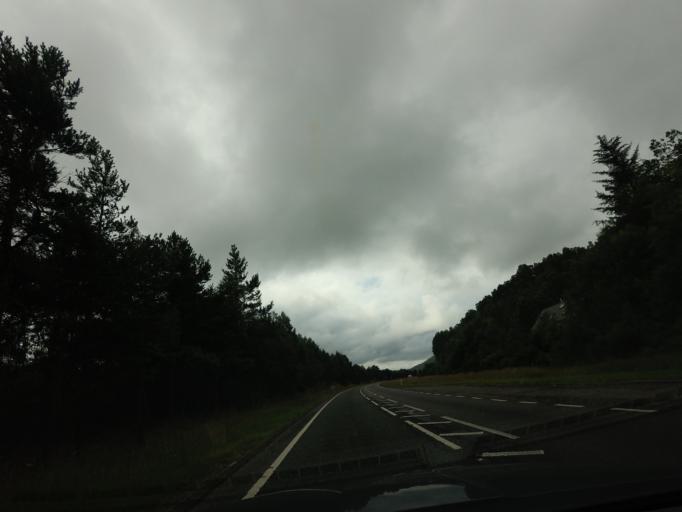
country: GB
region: Scotland
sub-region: Highland
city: Aviemore
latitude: 57.1796
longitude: -3.8354
